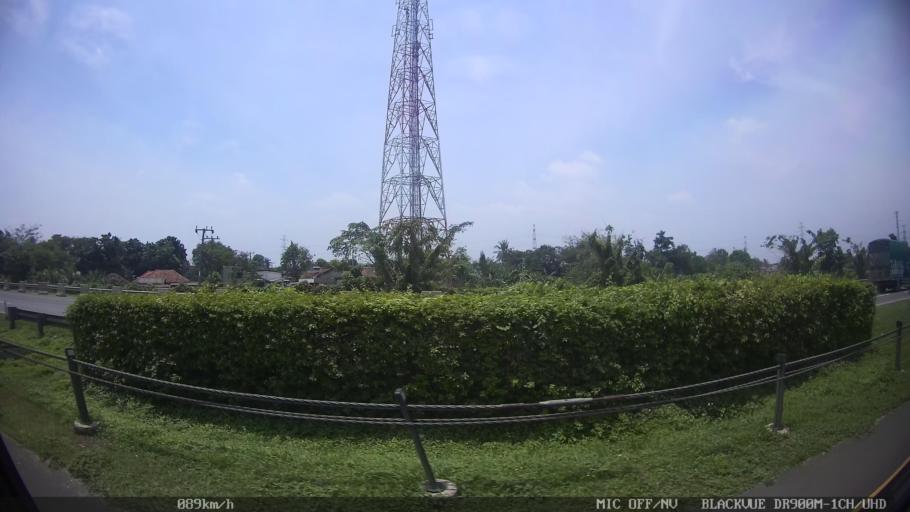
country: ID
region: West Java
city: Kresek
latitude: -6.1891
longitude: 106.4107
